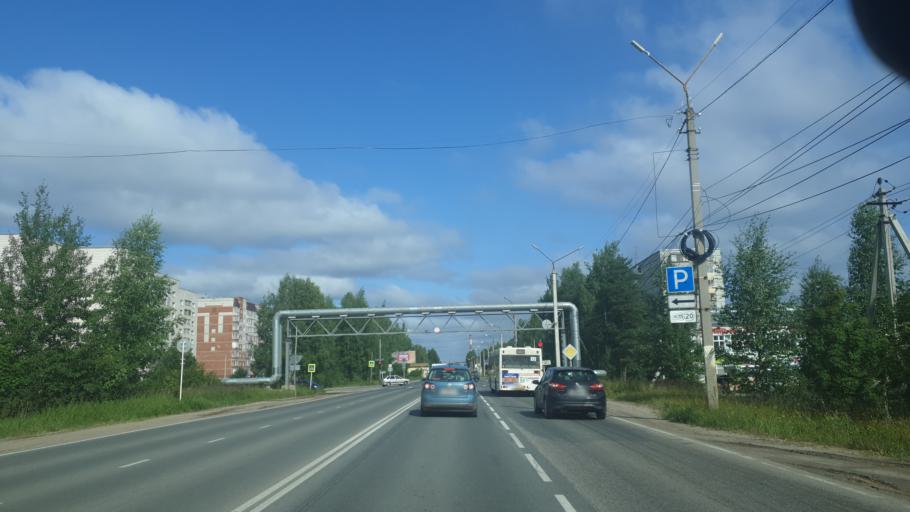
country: RU
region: Komi Republic
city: Ezhva
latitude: 61.7861
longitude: 50.7448
